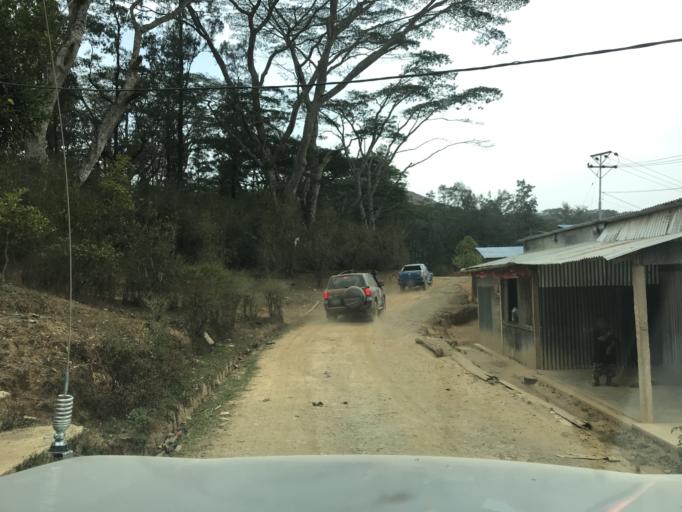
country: TL
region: Ermera
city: Gleno
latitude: -8.8334
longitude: 125.4511
